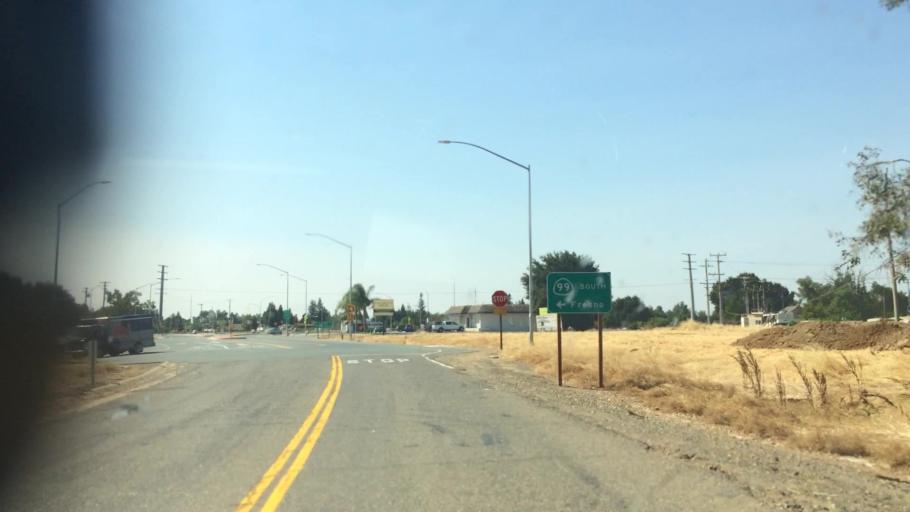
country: US
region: California
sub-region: Sacramento County
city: Galt
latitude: 38.2929
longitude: -121.3141
